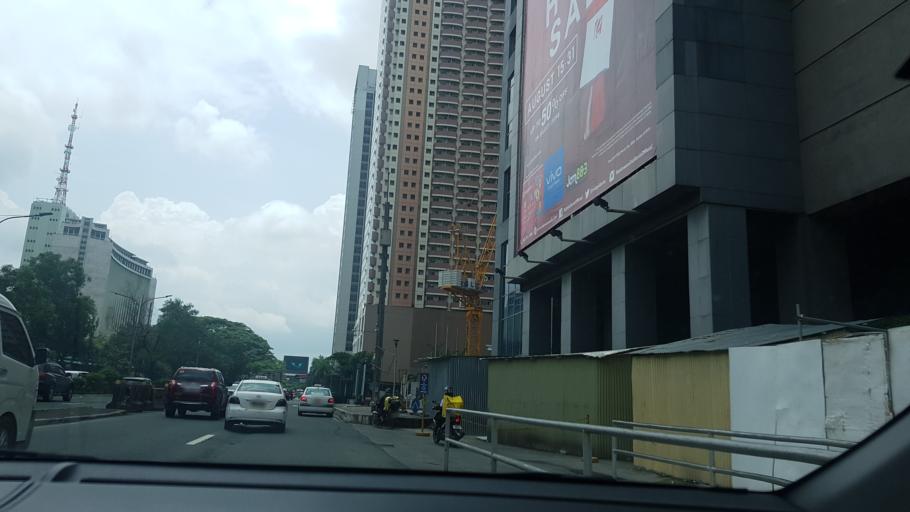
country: PH
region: Metro Manila
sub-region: Pasig
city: Pasig City
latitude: 14.5912
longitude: 121.0606
